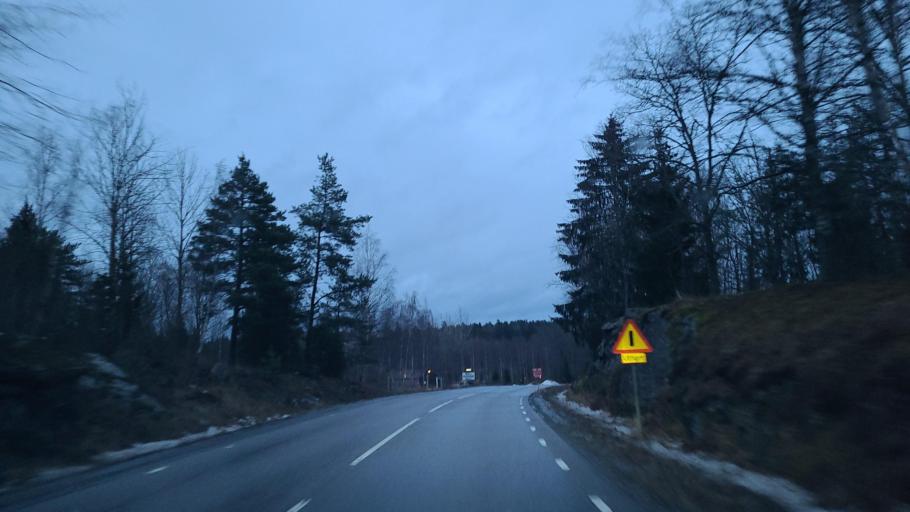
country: SE
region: Stockholm
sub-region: Norrtalje Kommun
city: Norrtalje
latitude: 59.7405
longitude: 18.6466
